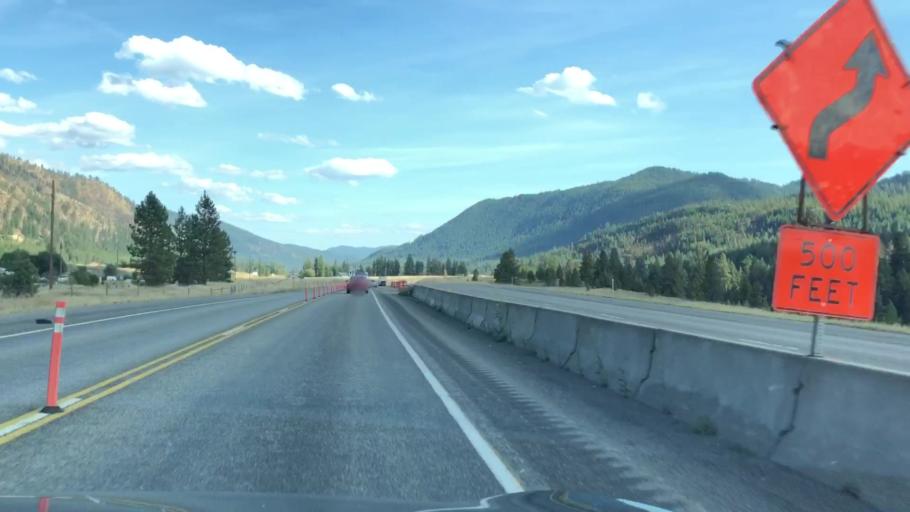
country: US
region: Montana
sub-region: Mineral County
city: Superior
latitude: 47.2141
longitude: -114.9431
